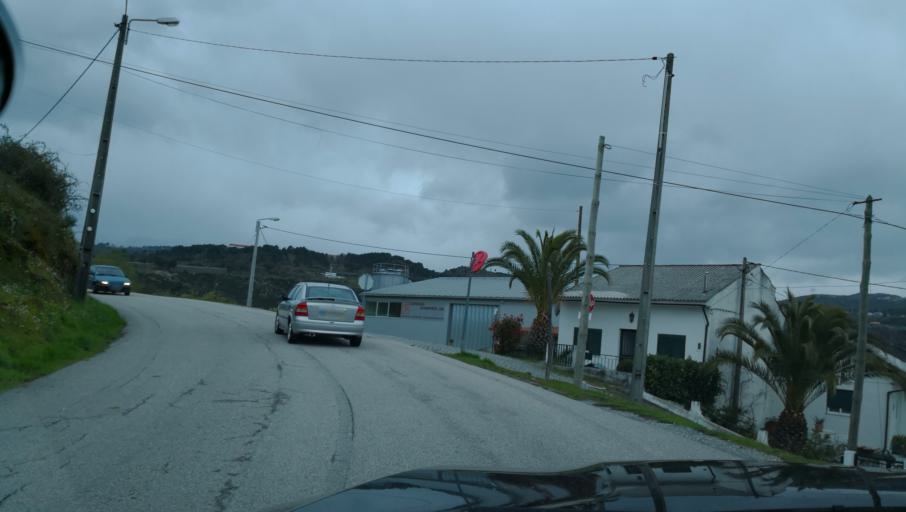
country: PT
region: Vila Real
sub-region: Vila Real
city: Vila Real
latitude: 41.2786
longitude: -7.7798
